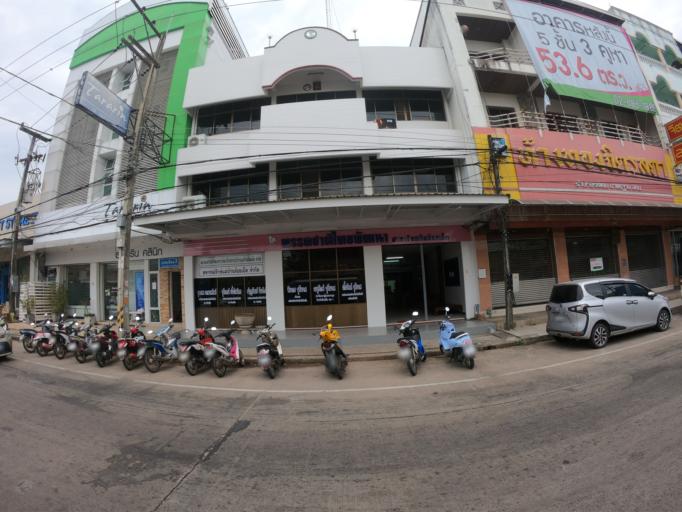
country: TH
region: Roi Et
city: Roi Et
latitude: 16.0579
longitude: 103.6569
